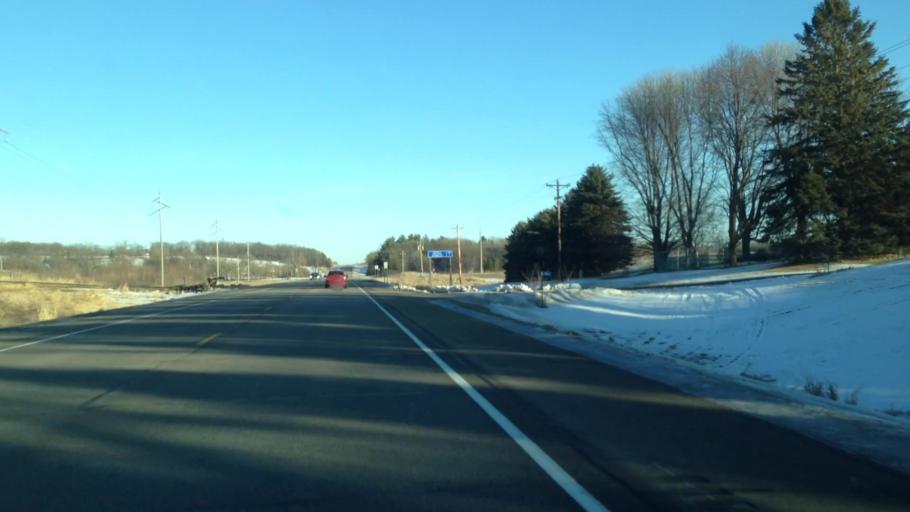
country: US
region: Minnesota
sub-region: Rice County
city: Lonsdale
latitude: 44.4792
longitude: -93.3768
